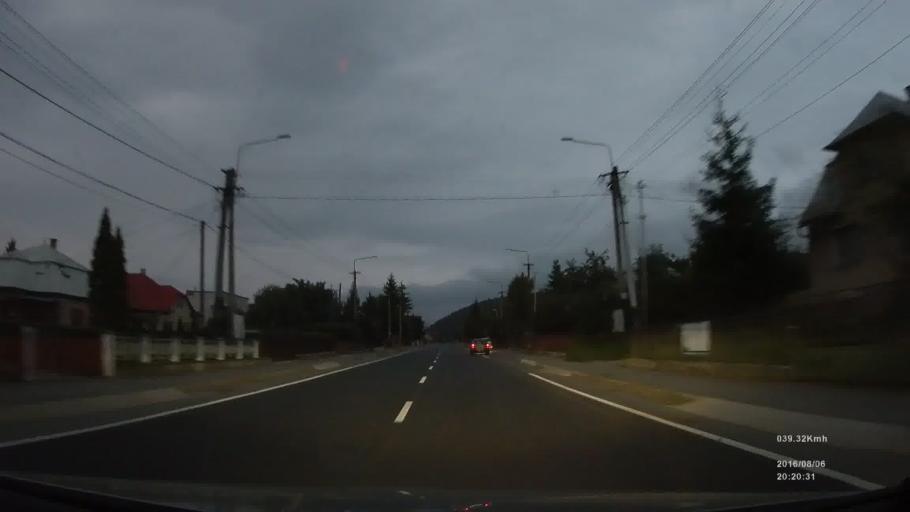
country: SK
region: Presovsky
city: Stropkov
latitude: 49.2144
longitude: 21.6574
